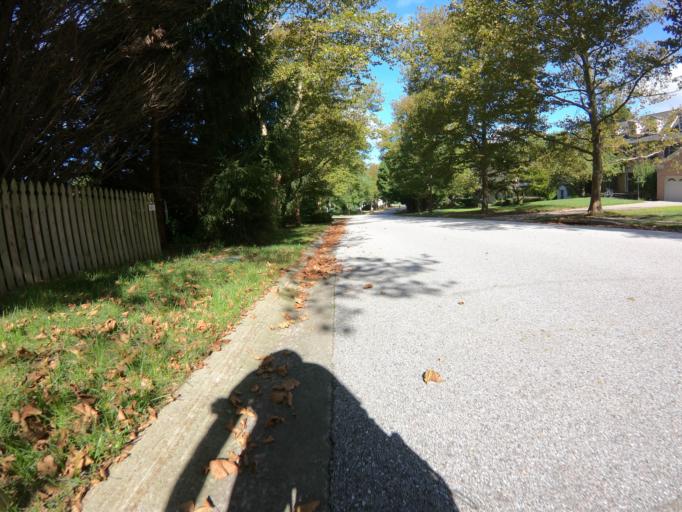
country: US
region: Maryland
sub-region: Howard County
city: Columbia
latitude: 39.2610
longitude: -76.8703
